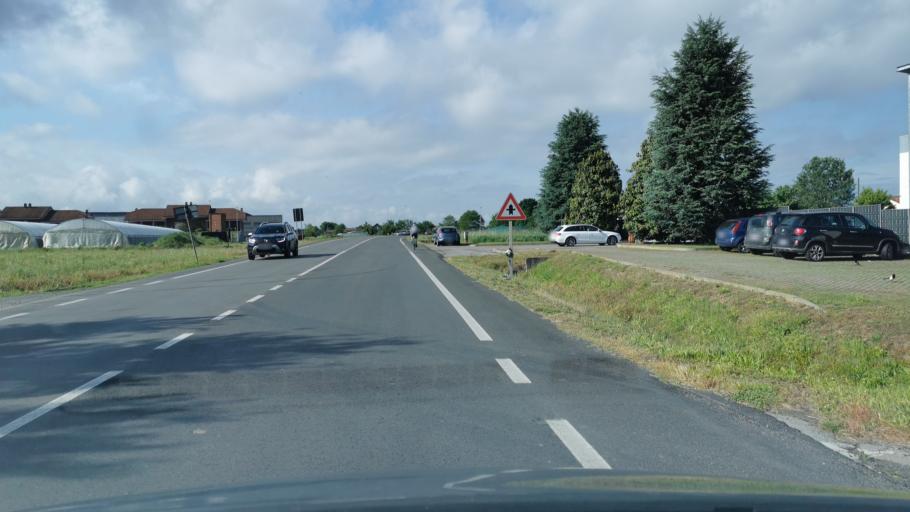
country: IT
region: Piedmont
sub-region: Provincia di Torino
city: Santena
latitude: 44.9443
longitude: 7.7820
